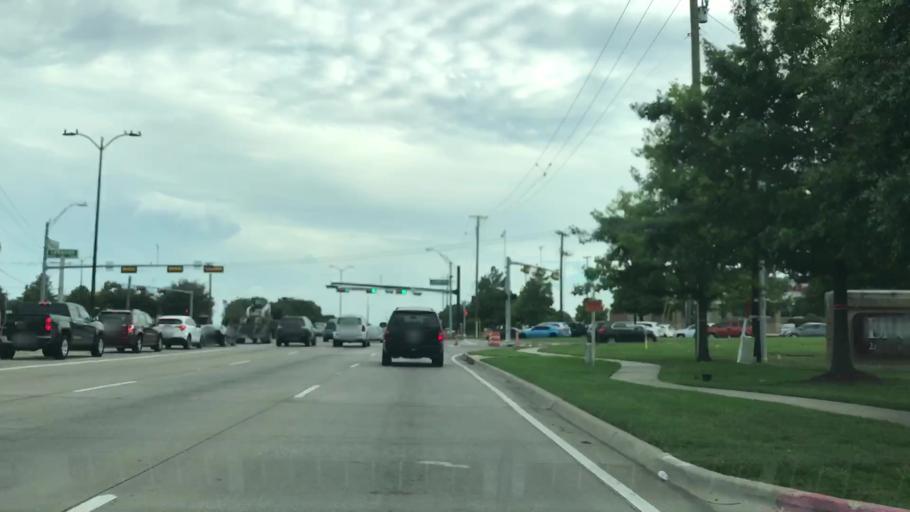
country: US
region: Texas
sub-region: Collin County
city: Frisco
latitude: 33.1219
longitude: -96.8057
